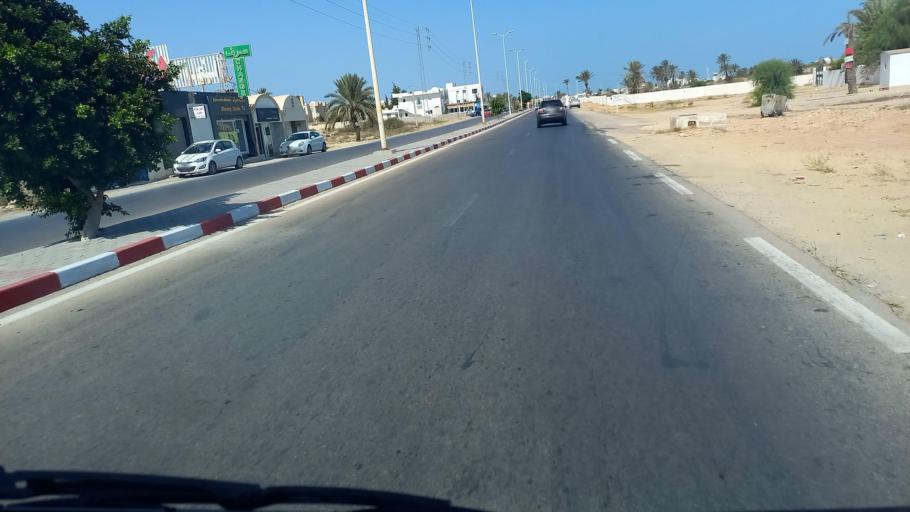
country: TN
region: Madanin
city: Midoun
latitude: 33.8609
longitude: 10.9688
